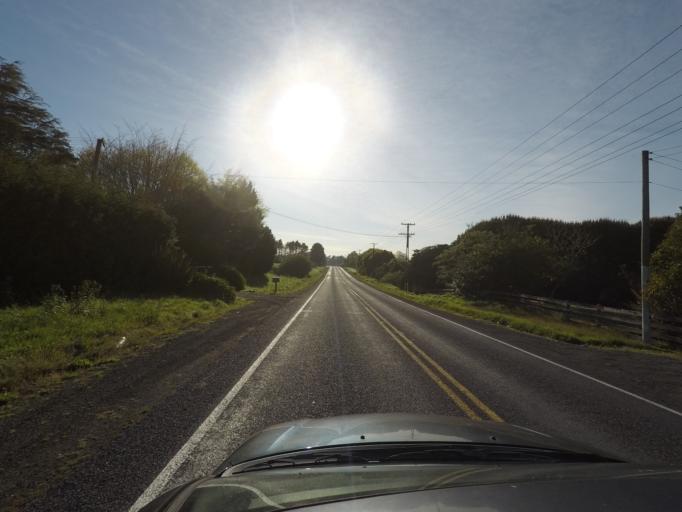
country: NZ
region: Auckland
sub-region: Auckland
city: Takanini
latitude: -37.0182
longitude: 174.9319
